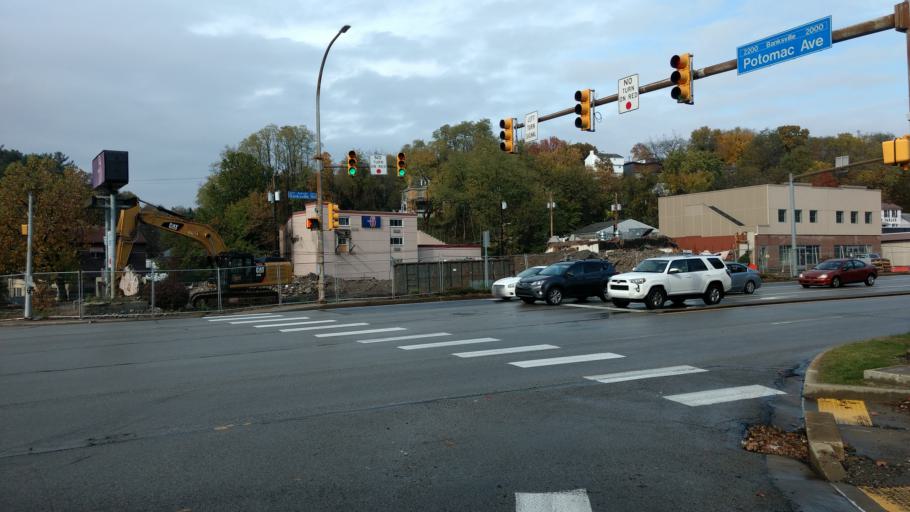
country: US
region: Pennsylvania
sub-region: Allegheny County
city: Dormont
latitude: 40.4029
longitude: -80.0405
